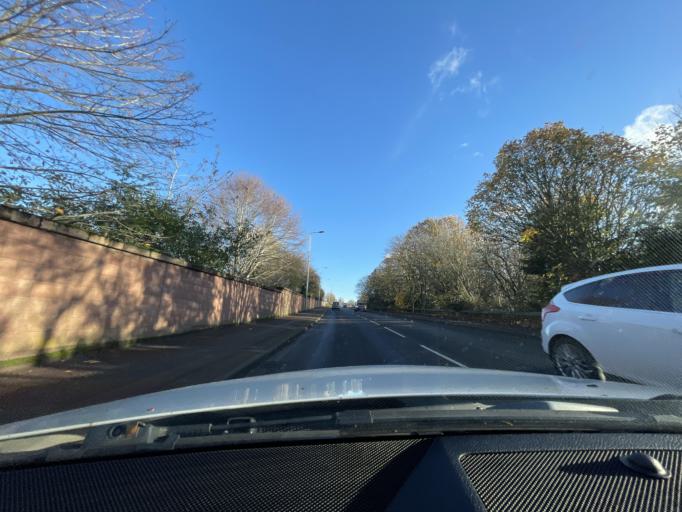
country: GB
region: Scotland
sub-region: Highland
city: Inverness
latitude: 57.4495
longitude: -4.2472
